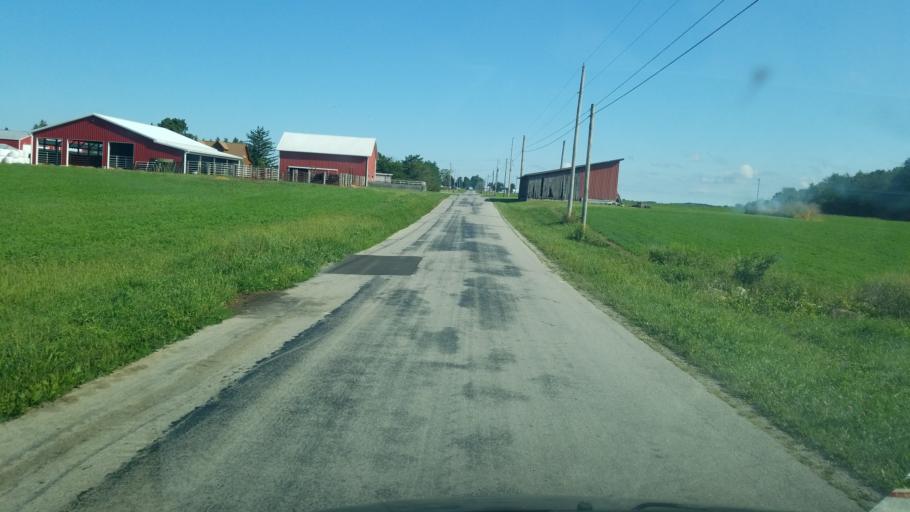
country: US
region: Ohio
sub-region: Wyandot County
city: Carey
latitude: 40.9616
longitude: -83.3338
